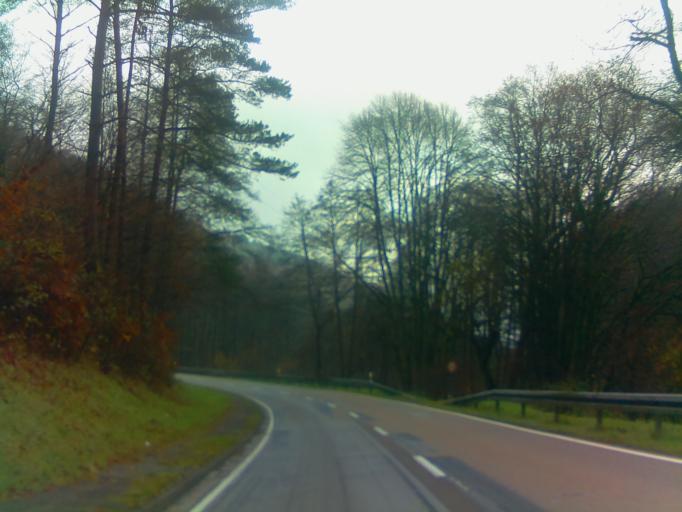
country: DE
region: Hesse
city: Hirschhorn
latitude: 49.4596
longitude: 8.8962
